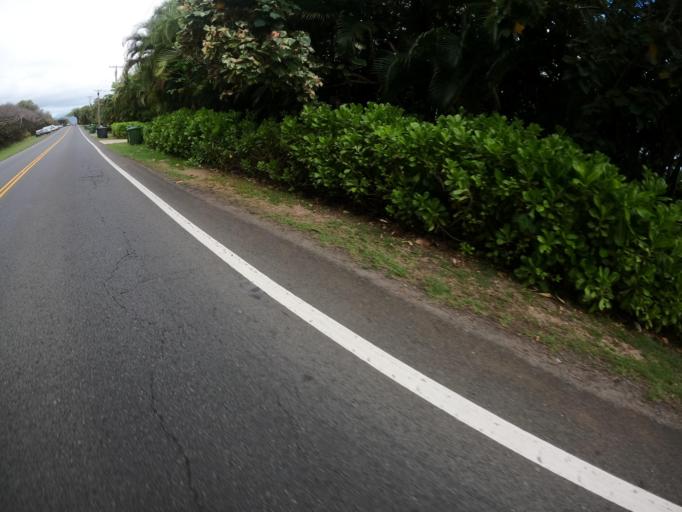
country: US
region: Hawaii
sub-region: Honolulu County
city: Waimanalo Beach
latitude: 21.3229
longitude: -157.6768
